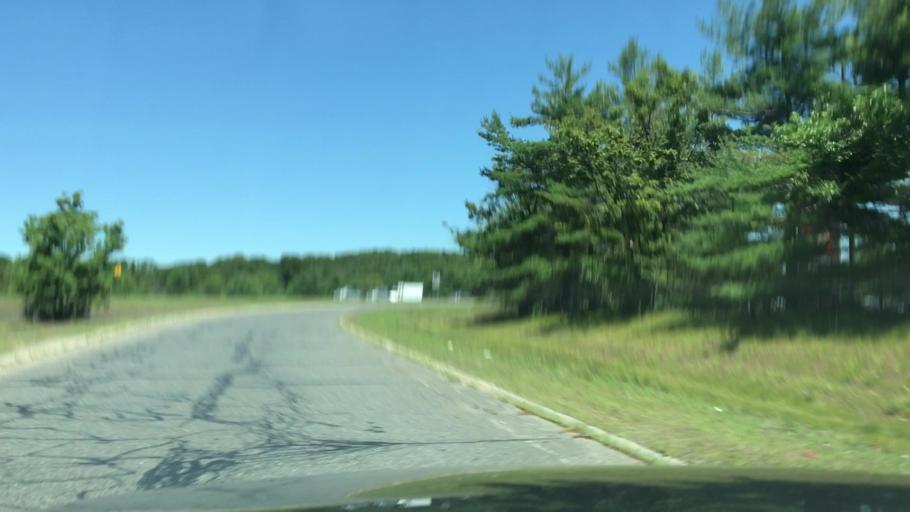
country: US
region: Massachusetts
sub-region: Bristol County
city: North Seekonk
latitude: 41.9023
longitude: -71.3532
